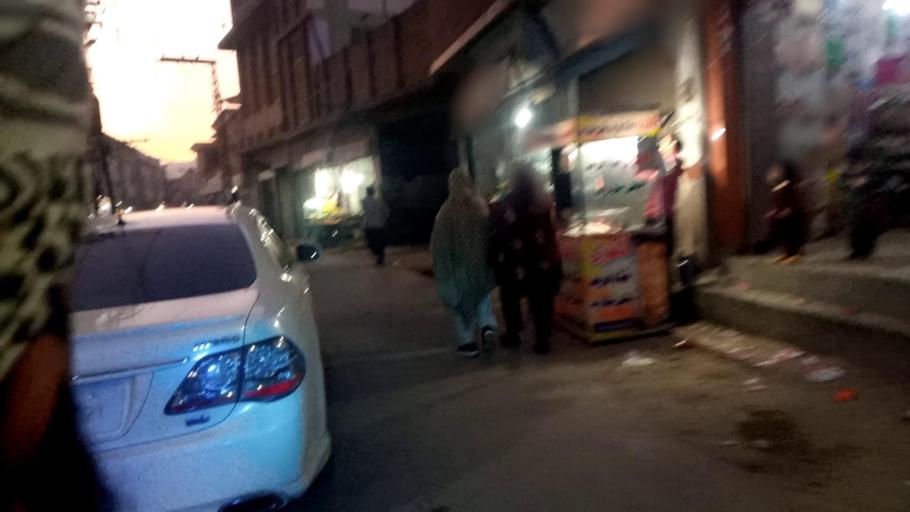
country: PK
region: Khyber Pakhtunkhwa
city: Mingora
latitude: 34.7772
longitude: 72.3494
